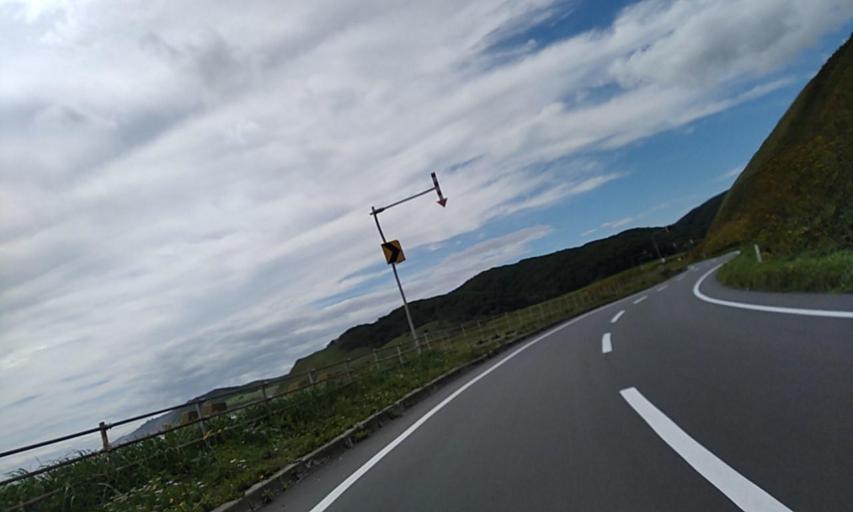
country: JP
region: Hokkaido
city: Kushiro
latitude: 42.7921
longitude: 143.8025
